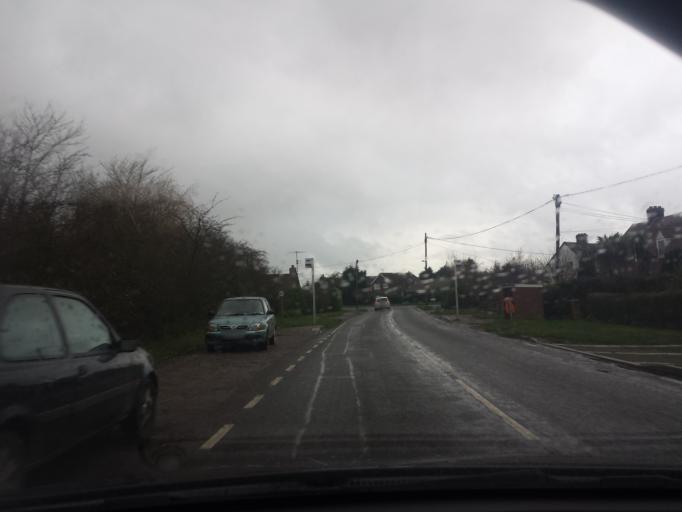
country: GB
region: England
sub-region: Essex
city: Dovercourt
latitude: 51.9072
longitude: 1.1992
